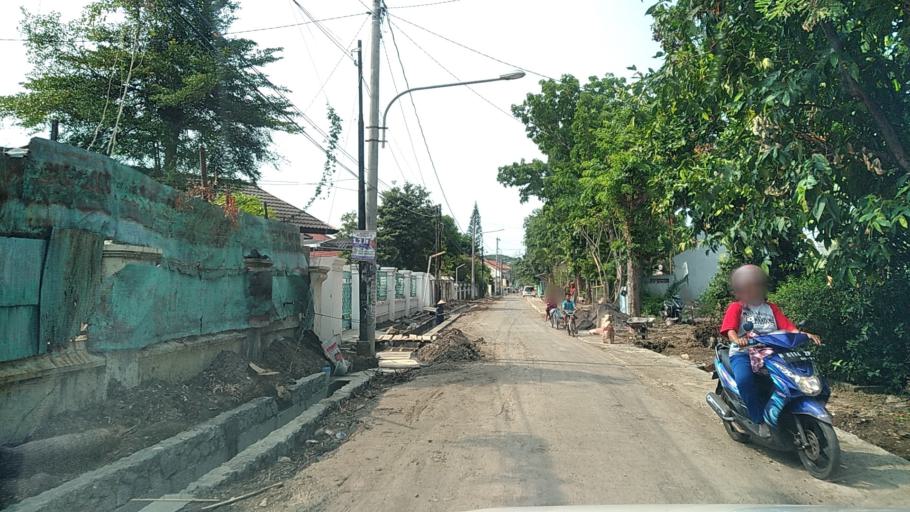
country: ID
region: Central Java
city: Semarang
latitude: -6.9965
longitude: 110.4506
